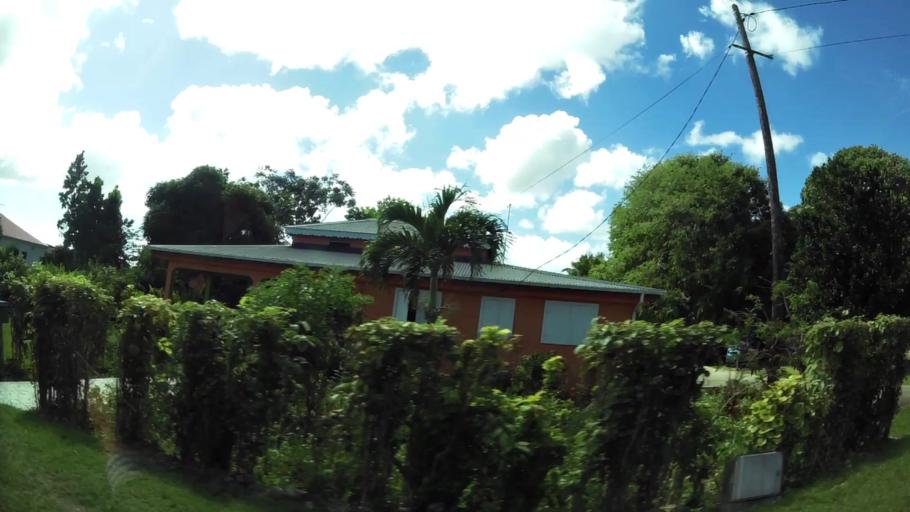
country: GP
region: Guadeloupe
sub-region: Guadeloupe
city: Le Moule
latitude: 16.3430
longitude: -61.4088
